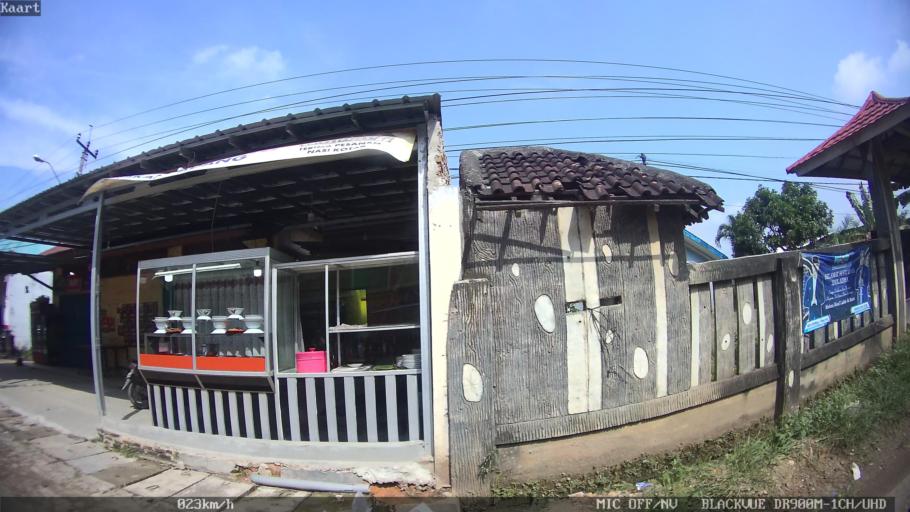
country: ID
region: Lampung
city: Kedaton
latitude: -5.3566
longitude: 105.2615
